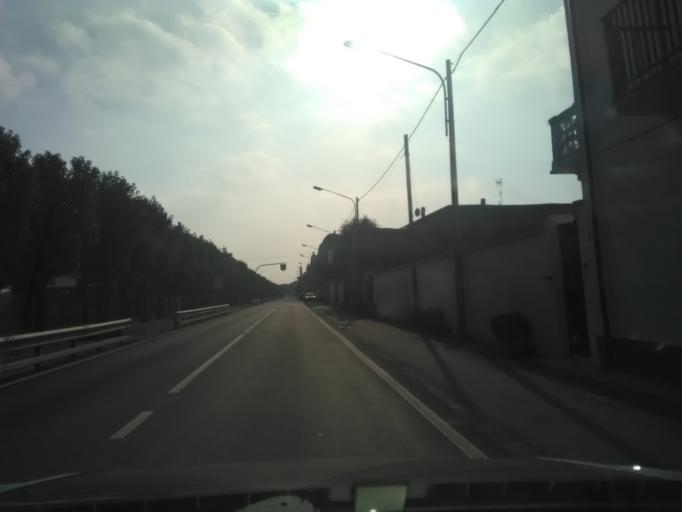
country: IT
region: Piedmont
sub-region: Provincia di Vercelli
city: Borgo d'Ale
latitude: 45.3545
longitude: 8.0578
